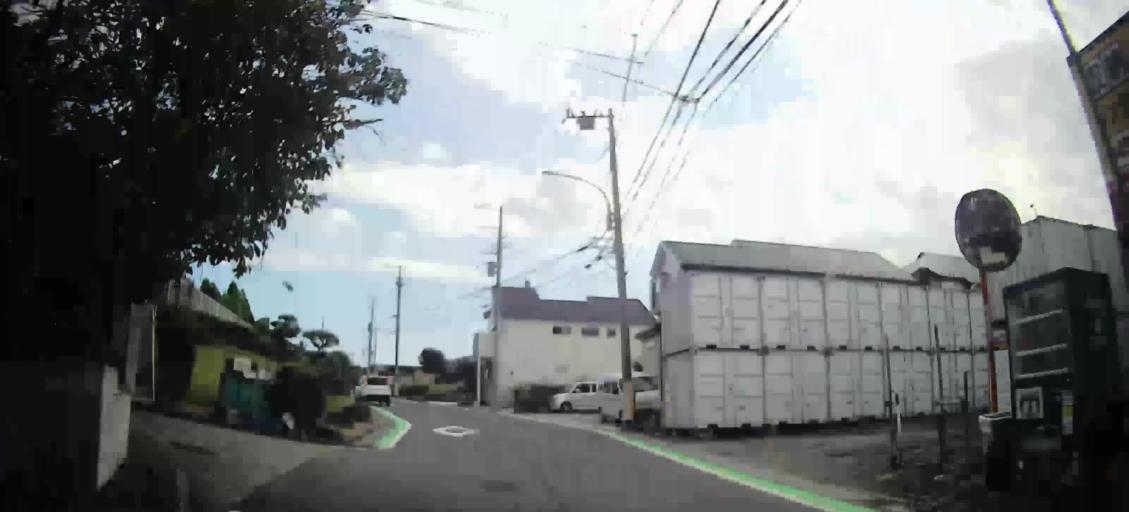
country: JP
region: Kanagawa
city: Yokohama
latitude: 35.4871
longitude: 139.5749
